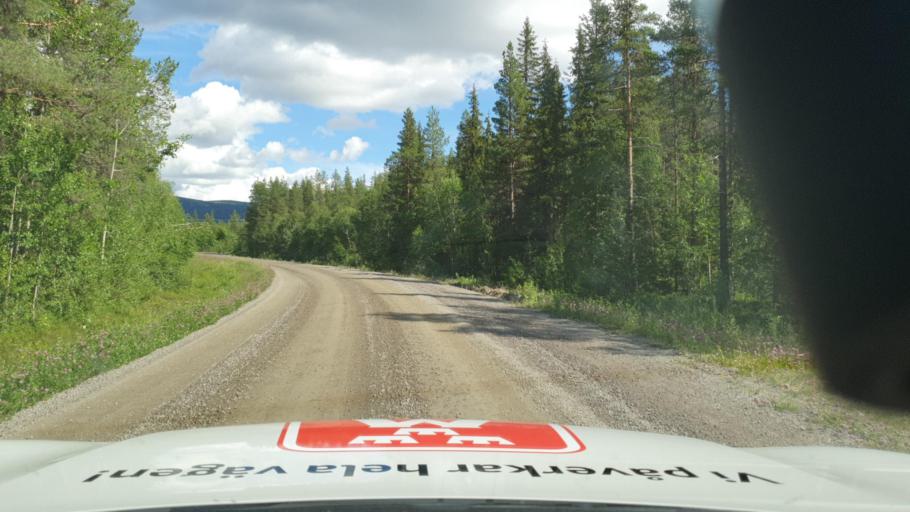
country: SE
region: Vaesterbotten
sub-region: Sorsele Kommun
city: Sorsele
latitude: 65.6297
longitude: 17.4241
